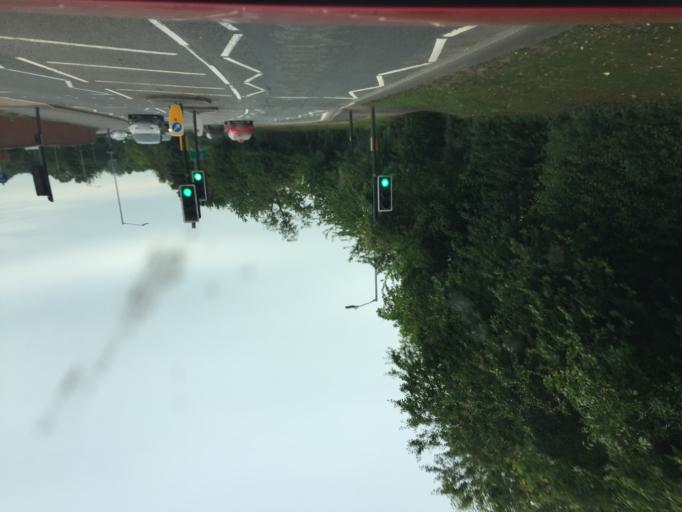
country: GB
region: England
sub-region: Warwickshire
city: Nuneaton
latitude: 52.5209
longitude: -1.4705
